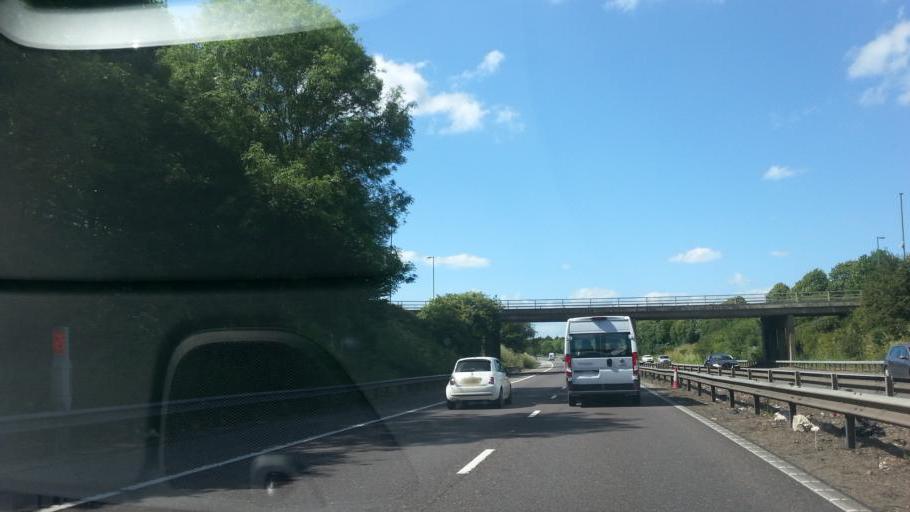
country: GB
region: England
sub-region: Hertfordshire
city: Stevenage
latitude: 51.8873
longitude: -0.2062
